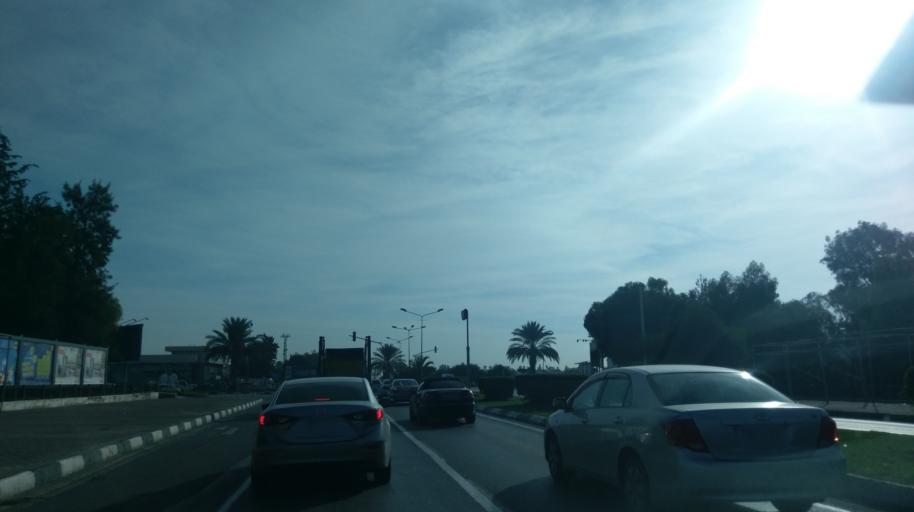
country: CY
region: Lefkosia
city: Nicosia
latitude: 35.2116
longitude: 33.3379
